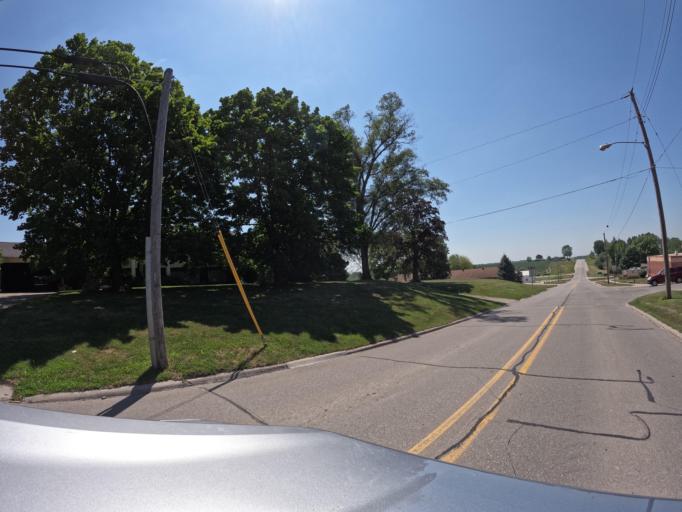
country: US
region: Iowa
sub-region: Keokuk County
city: Sigourney
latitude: 41.3234
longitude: -92.2052
